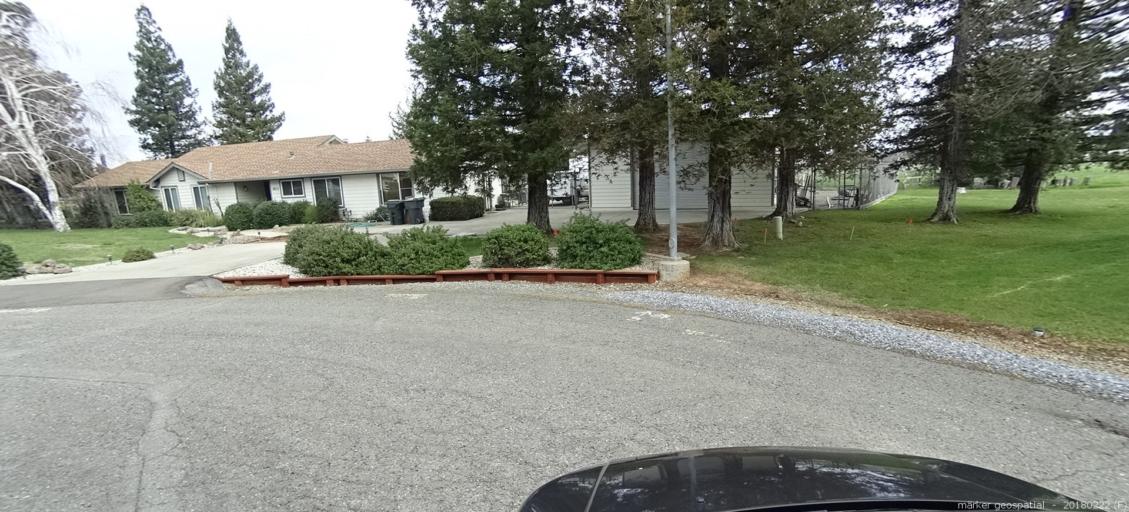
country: US
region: California
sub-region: Sacramento County
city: Rio Linda
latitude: 38.7130
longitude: -121.4180
